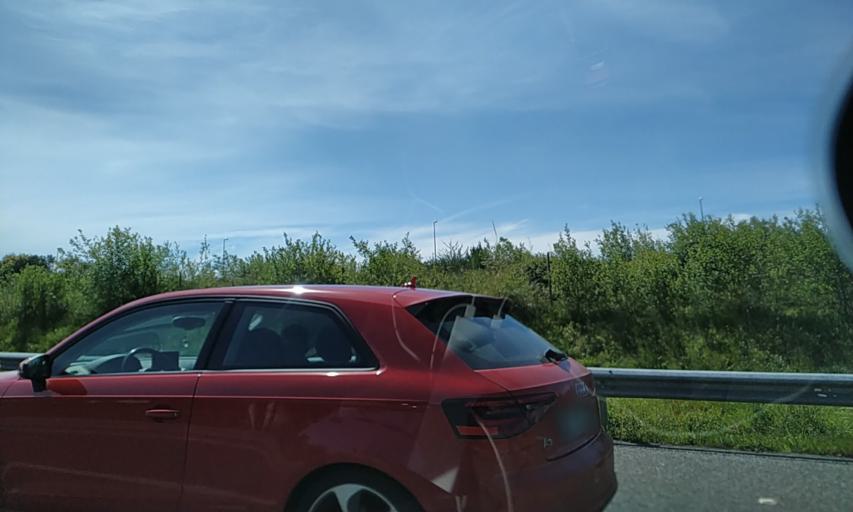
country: ES
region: Galicia
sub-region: Provincia de Pontevedra
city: Sanxenxo
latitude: 42.4286
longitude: -8.8056
